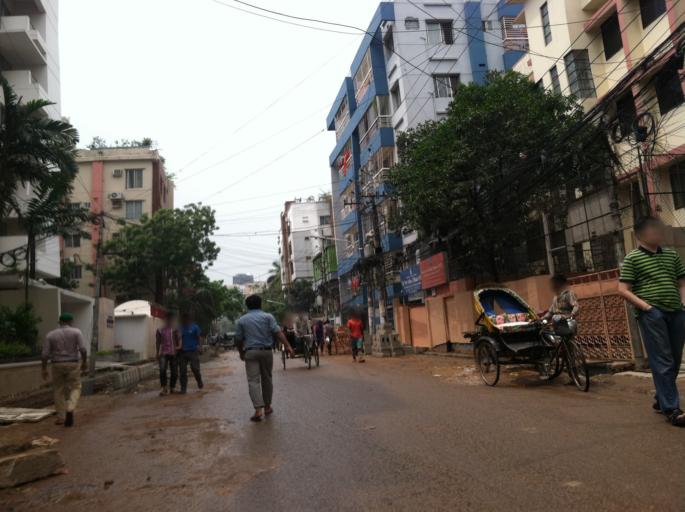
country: BD
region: Dhaka
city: Paltan
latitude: 23.7861
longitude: 90.4031
